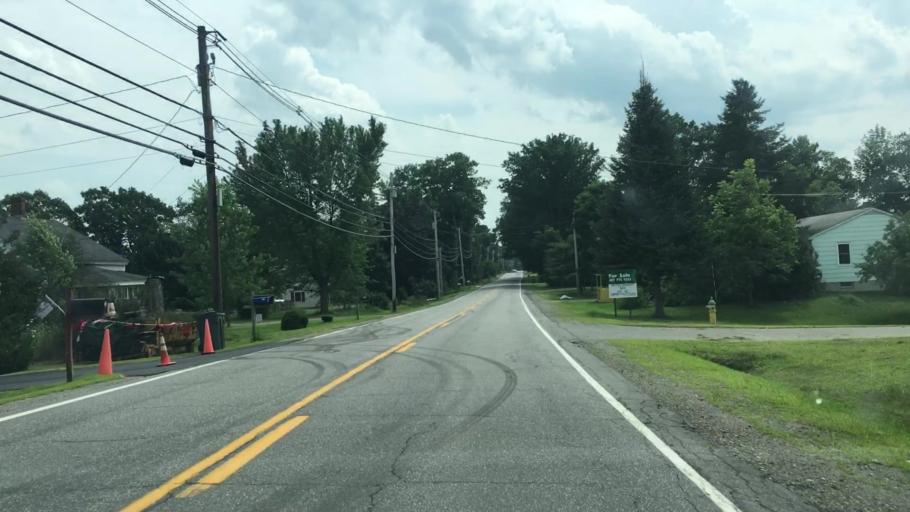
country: US
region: Maine
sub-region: Kennebec County
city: Winslow
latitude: 44.5081
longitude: -69.6312
